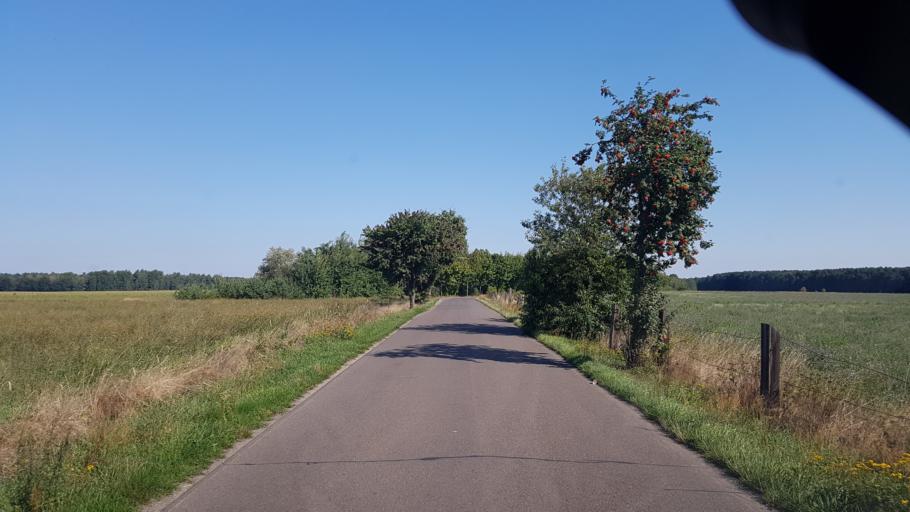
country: DE
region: Brandenburg
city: Vetschau
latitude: 51.7542
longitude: 14.0394
